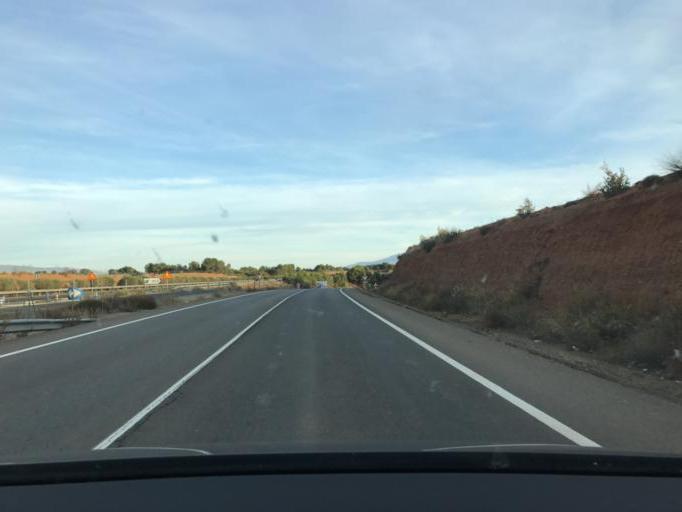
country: ES
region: Andalusia
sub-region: Provincia de Granada
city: Albunan
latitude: 37.2640
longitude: -3.0891
